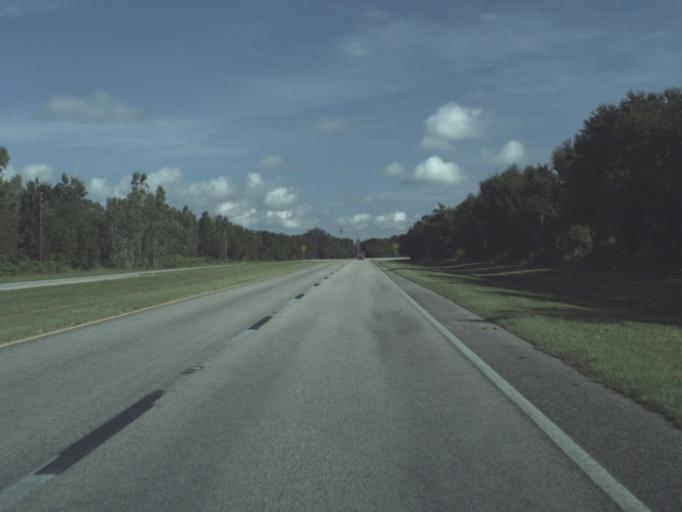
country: US
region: Florida
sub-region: Hardee County
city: Bowling Green
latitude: 27.6724
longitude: -81.8220
